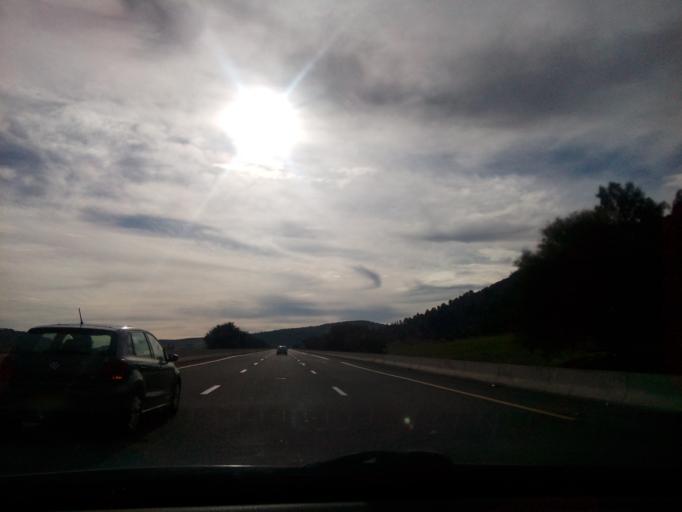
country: DZ
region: Sidi Bel Abbes
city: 'Ain el Berd
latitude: 35.3998
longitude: -0.4914
